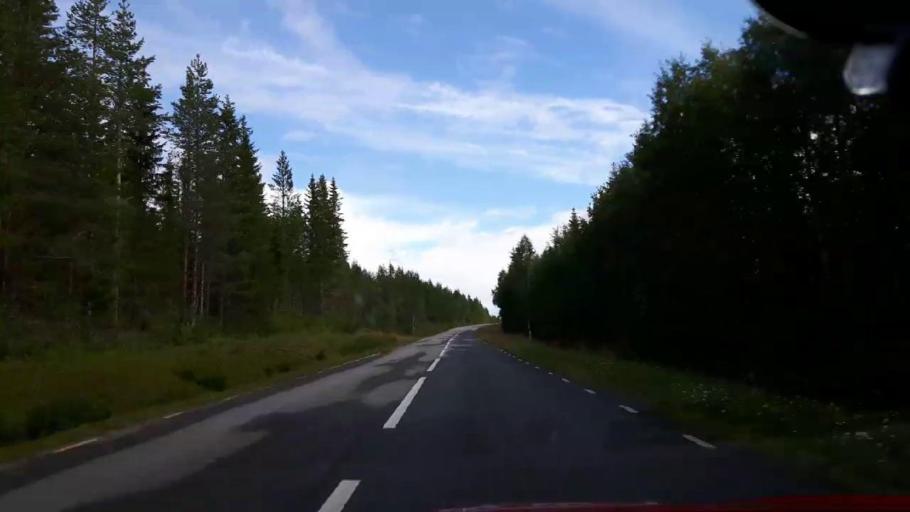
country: SE
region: Jaemtland
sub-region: Stroemsunds Kommun
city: Stroemsund
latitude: 64.3468
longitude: 15.0867
